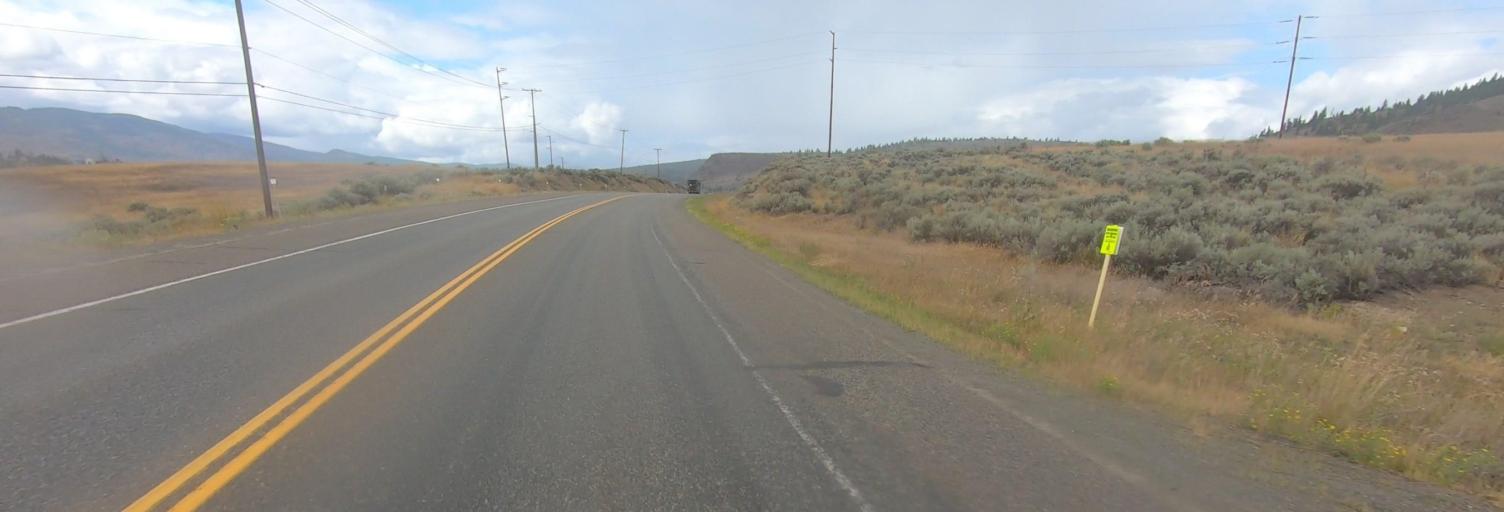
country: CA
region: British Columbia
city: Kamloops
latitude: 50.6669
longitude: -120.5005
